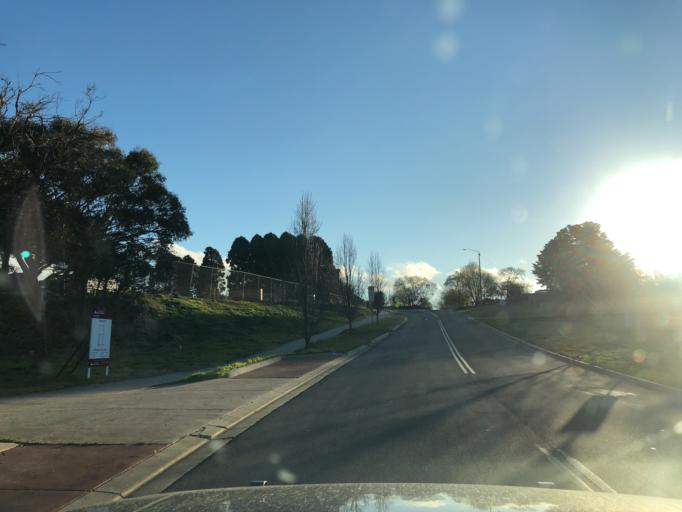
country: AU
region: Victoria
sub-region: Moorabool
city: Bacchus Marsh
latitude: -37.5990
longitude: 144.2297
